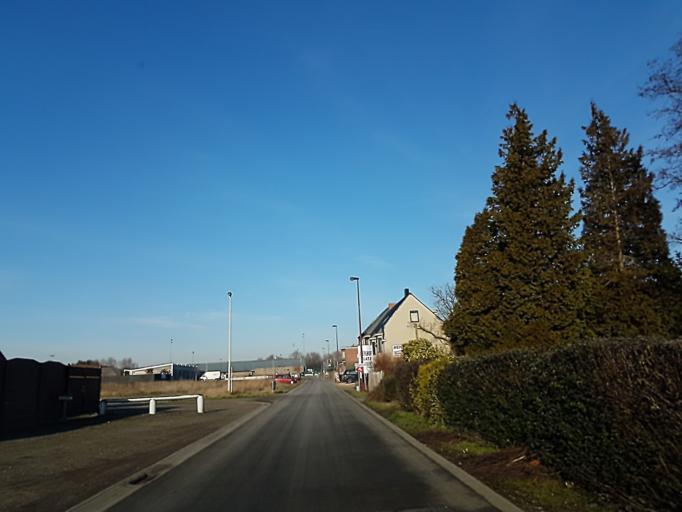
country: BE
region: Flanders
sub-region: Provincie Antwerpen
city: Hove
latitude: 51.1376
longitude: 4.4692
